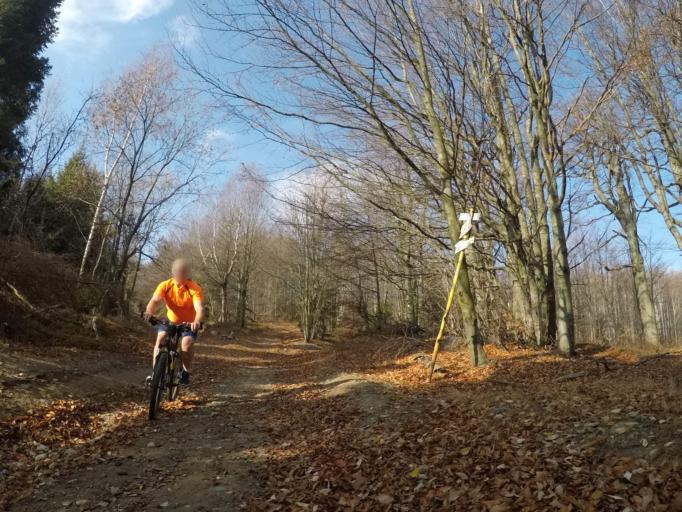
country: SK
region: Kosicky
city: Gelnica
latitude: 48.7650
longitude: 21.0260
